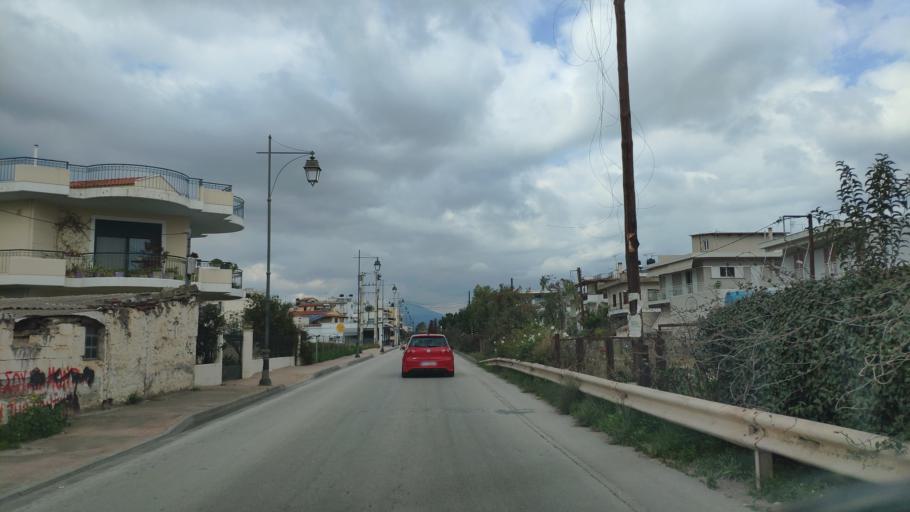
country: GR
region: Peloponnese
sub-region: Nomos Argolidos
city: Argos
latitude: 37.6396
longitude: 22.7334
